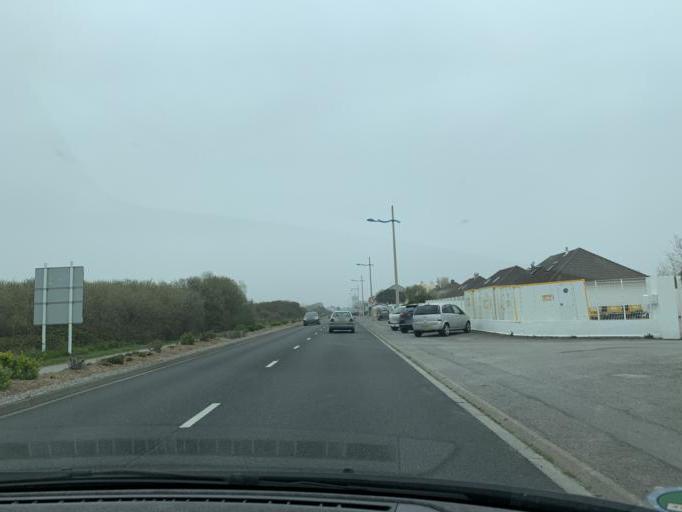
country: FR
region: Nord-Pas-de-Calais
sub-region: Departement du Pas-de-Calais
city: Coquelles
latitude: 50.9563
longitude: 1.8048
